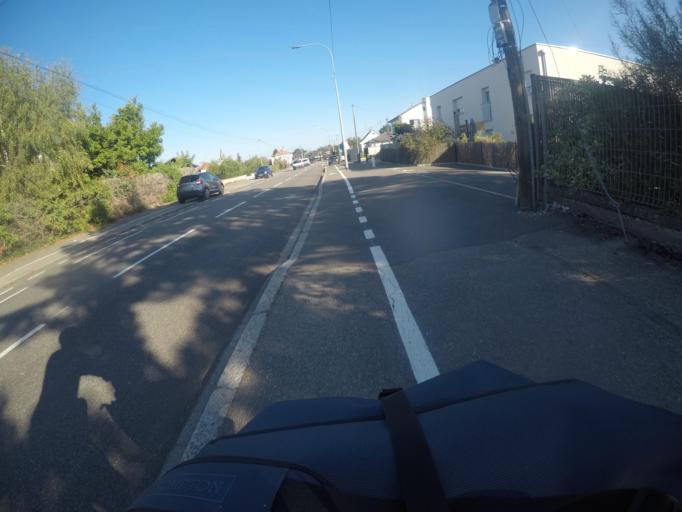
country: FR
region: Alsace
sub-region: Departement du Haut-Rhin
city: Rosenau
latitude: 47.6487
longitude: 7.5101
